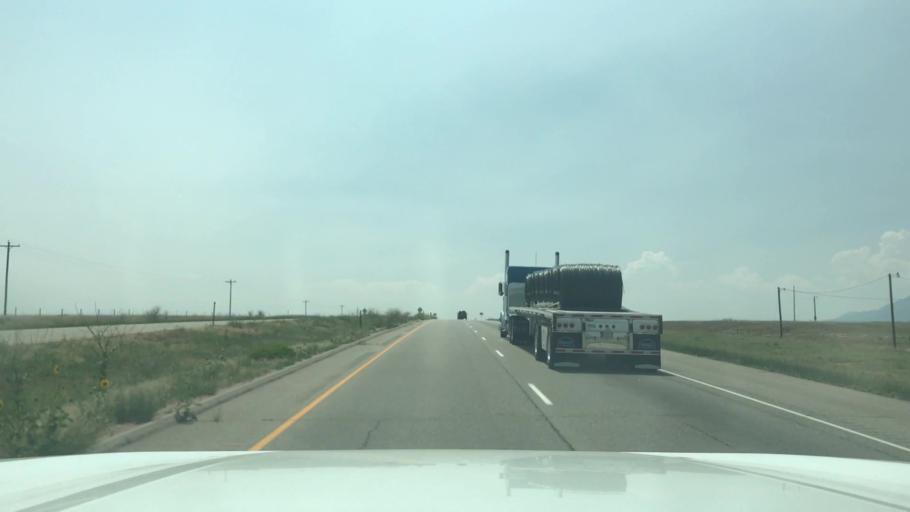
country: US
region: Colorado
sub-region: Pueblo County
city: Colorado City
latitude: 37.9340
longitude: -104.8181
